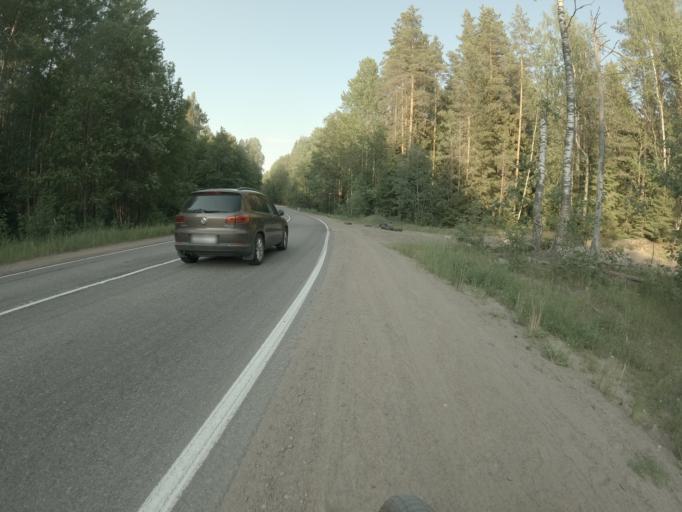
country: RU
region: Leningrad
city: Veshchevo
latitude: 60.4641
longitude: 29.2410
